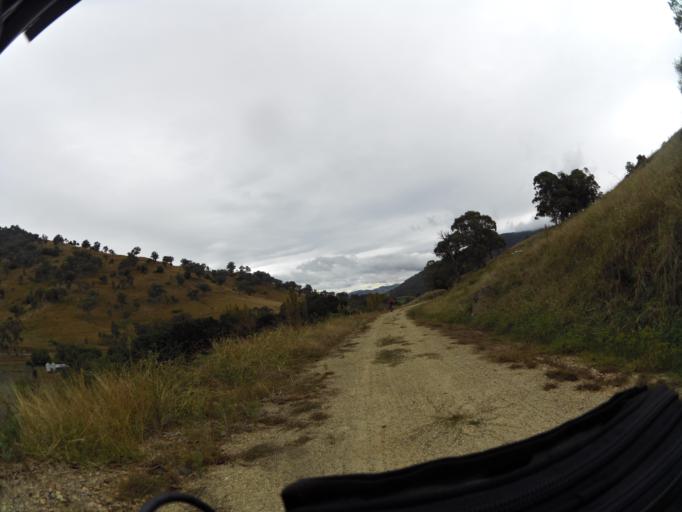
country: AU
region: New South Wales
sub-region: Albury Municipality
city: East Albury
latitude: -36.1856
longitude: 147.3571
